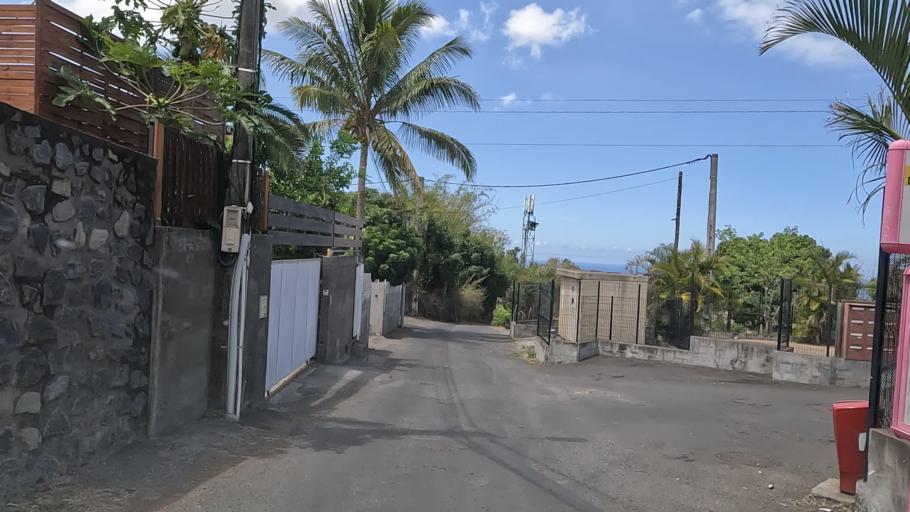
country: RE
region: Reunion
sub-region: Reunion
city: Saint-Louis
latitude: -21.2784
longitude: 55.4451
